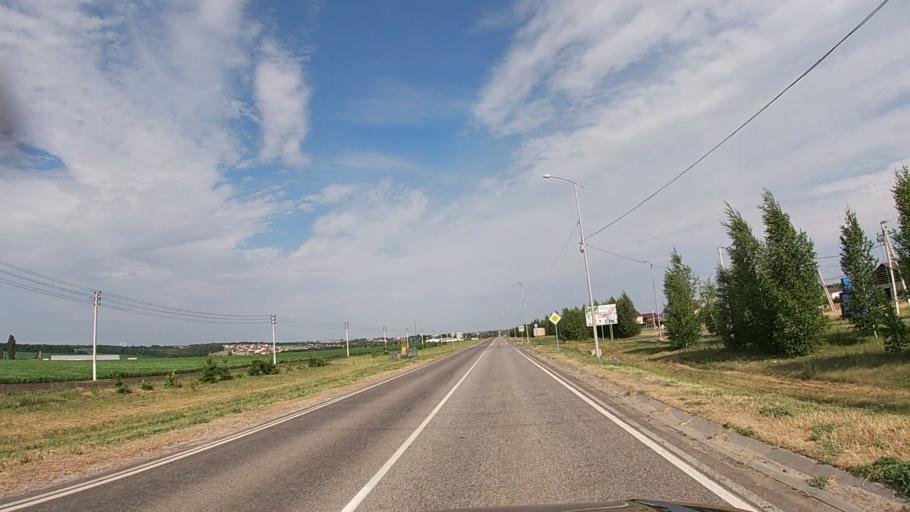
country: RU
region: Belgorod
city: Krasnaya Yaruga
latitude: 50.7967
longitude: 35.6904
